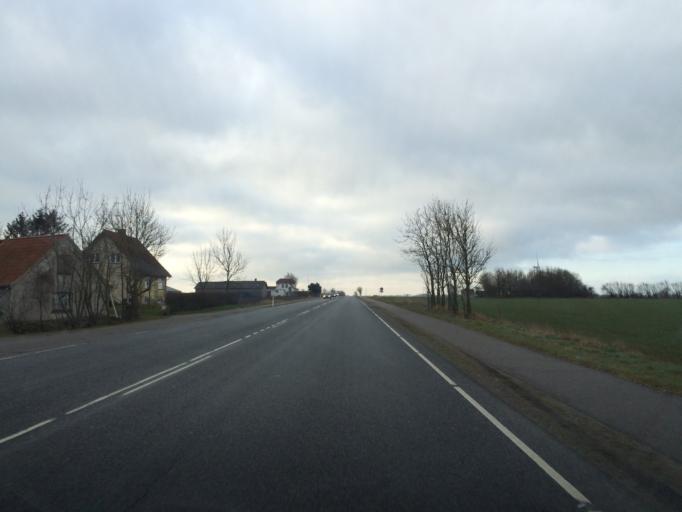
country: DK
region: South Denmark
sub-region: Fredericia Kommune
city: Taulov
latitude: 55.5805
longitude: 9.6598
